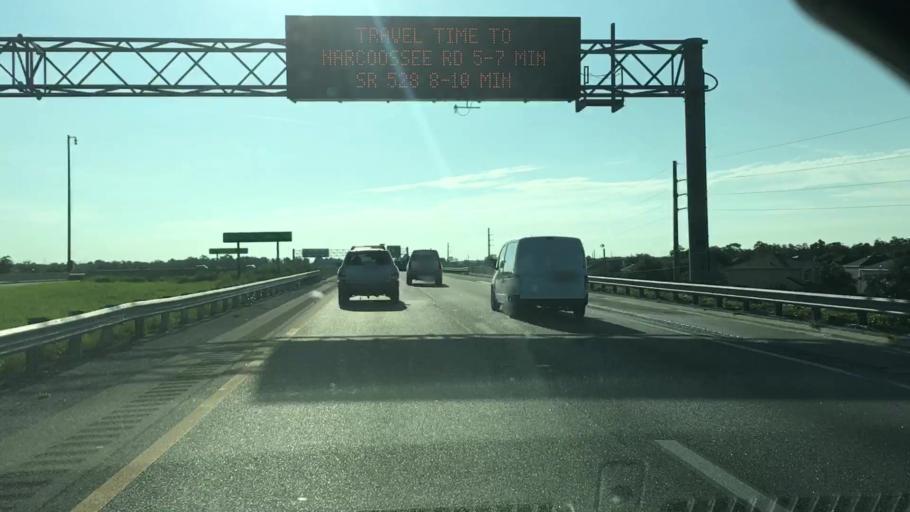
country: US
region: Florida
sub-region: Orange County
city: Meadow Woods
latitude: 28.3687
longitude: -81.3483
